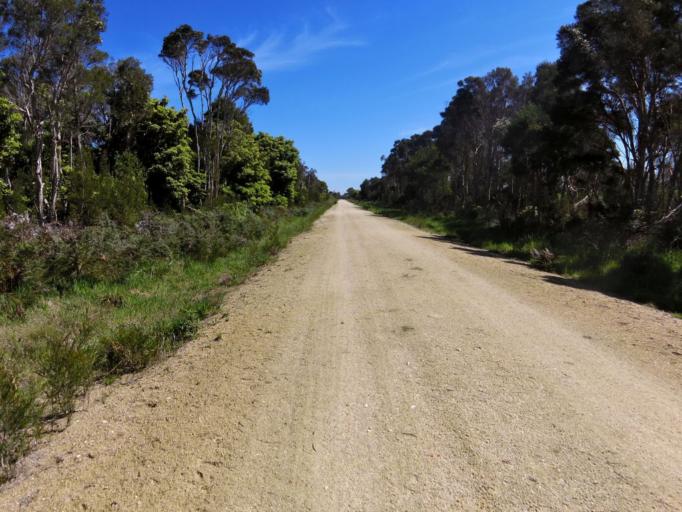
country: AU
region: Victoria
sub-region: Latrobe
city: Morwell
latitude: -38.6691
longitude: 146.4226
